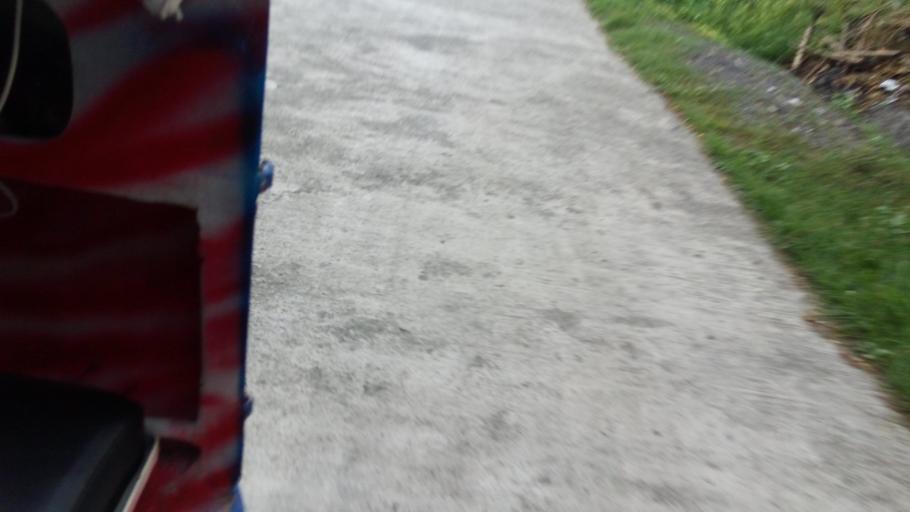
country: PH
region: Ilocos
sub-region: Province of La Union
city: Santo Tomas
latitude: 16.2916
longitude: 120.3786
